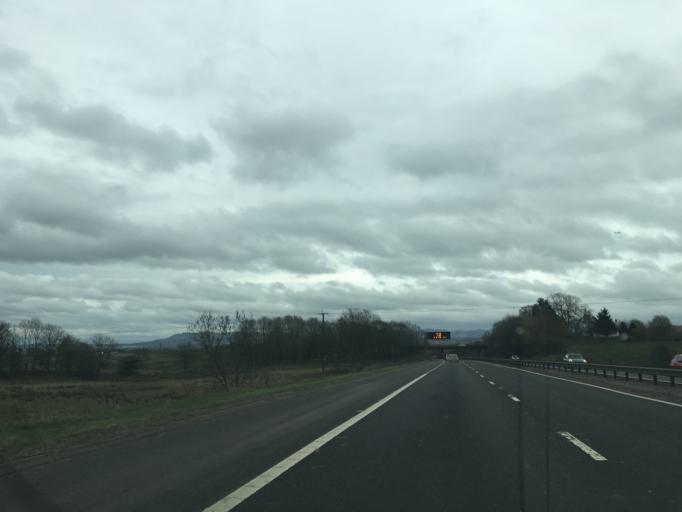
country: GB
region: Scotland
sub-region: West Lothian
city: Broxburn
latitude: 55.9645
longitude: -3.4457
